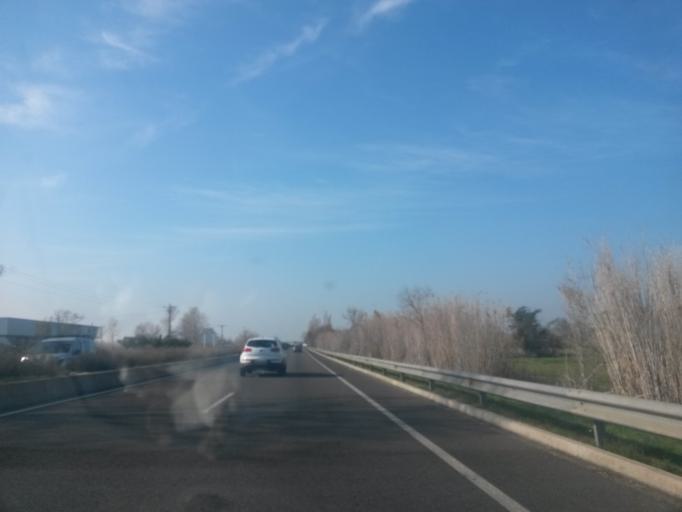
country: ES
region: Catalonia
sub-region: Provincia de Girona
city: Empuriabrava
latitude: 42.2652
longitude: 3.1166
